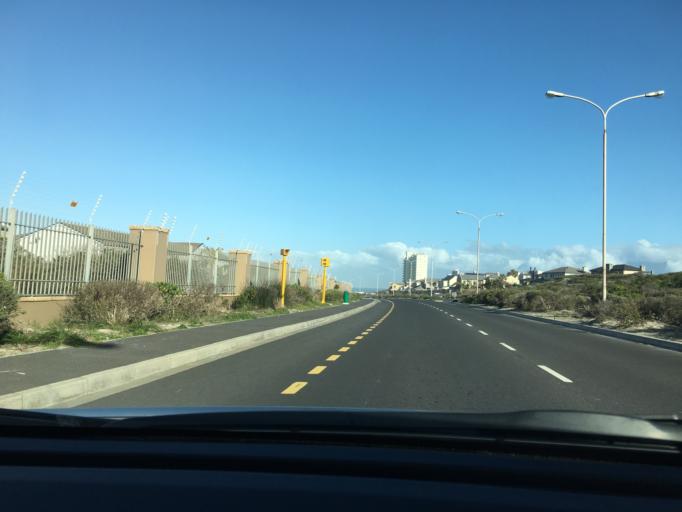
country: ZA
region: Western Cape
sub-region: City of Cape Town
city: Sunset Beach
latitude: -33.7970
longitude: 18.4619
